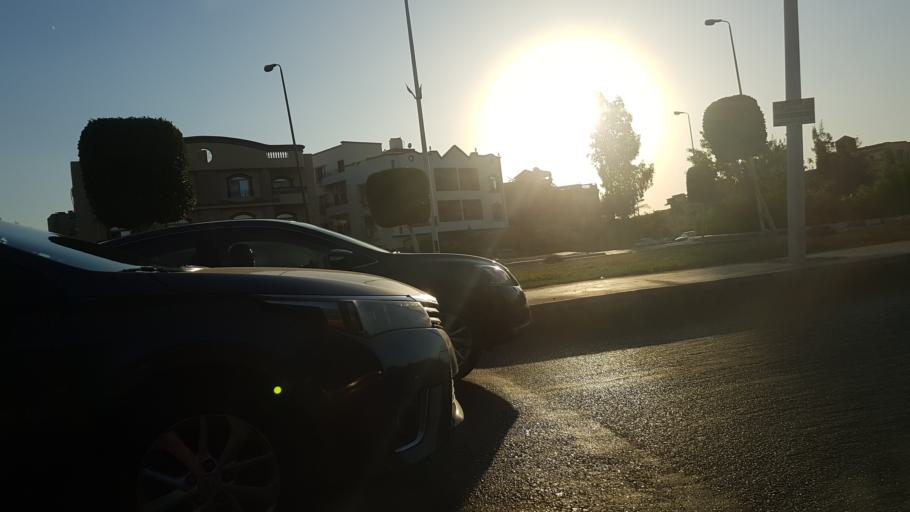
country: EG
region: Muhafazat al Qalyubiyah
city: Al Khankah
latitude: 30.0318
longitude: 31.4396
